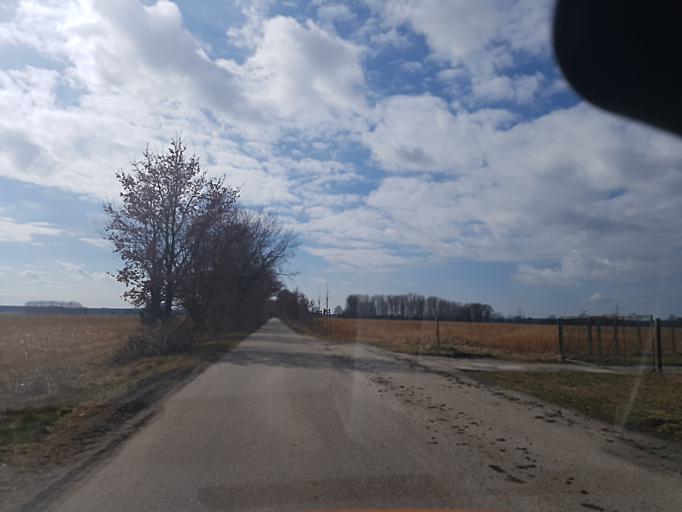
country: DE
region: Brandenburg
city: Ruckersdorf
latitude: 51.5863
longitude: 13.5382
